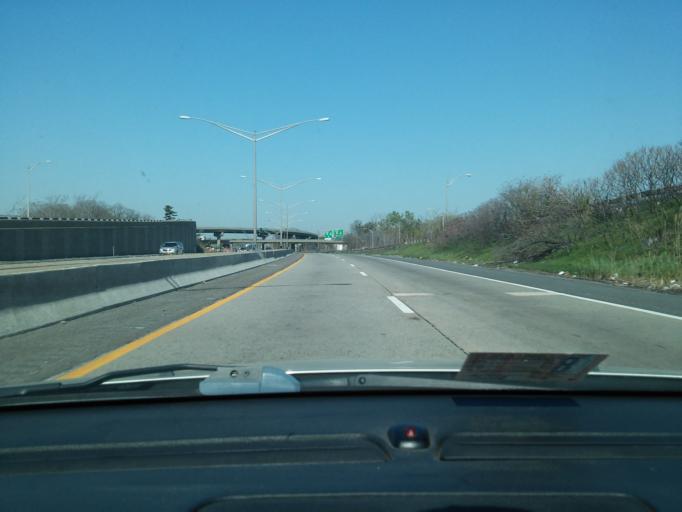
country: US
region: New Jersey
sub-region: Essex County
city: Newark
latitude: 40.7102
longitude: -74.1620
